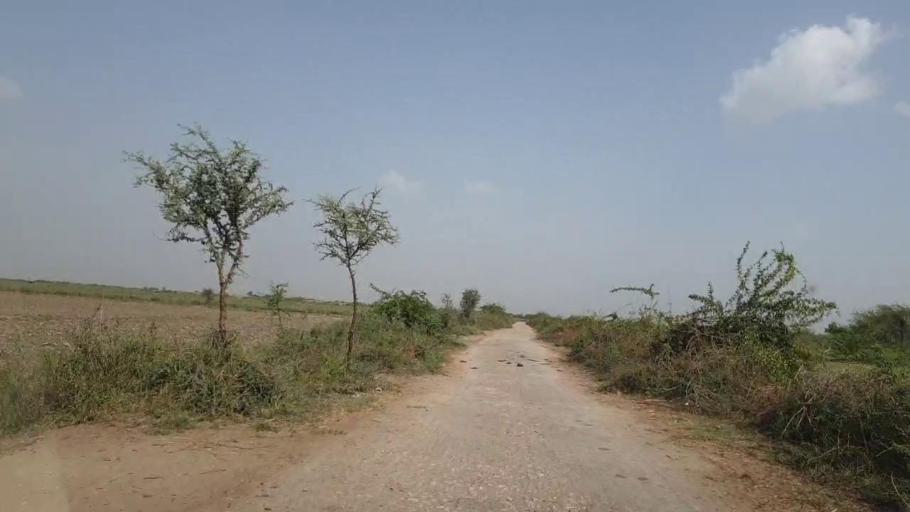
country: PK
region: Sindh
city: Rajo Khanani
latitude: 25.0327
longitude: 68.8744
